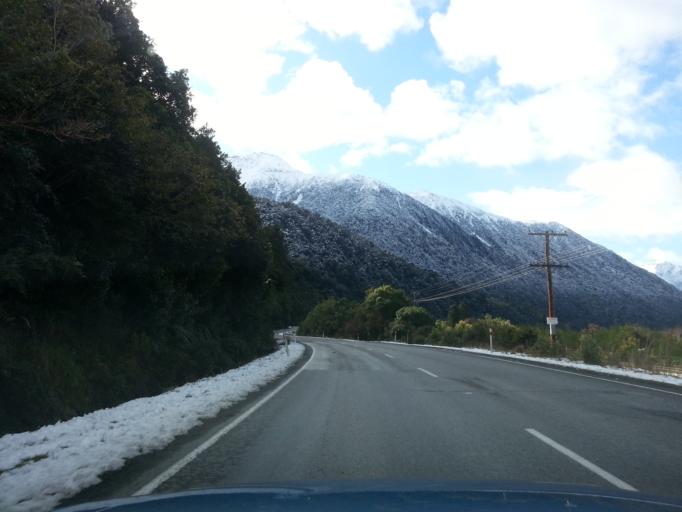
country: NZ
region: West Coast
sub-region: Grey District
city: Greymouth
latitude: -42.8152
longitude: 171.5653
